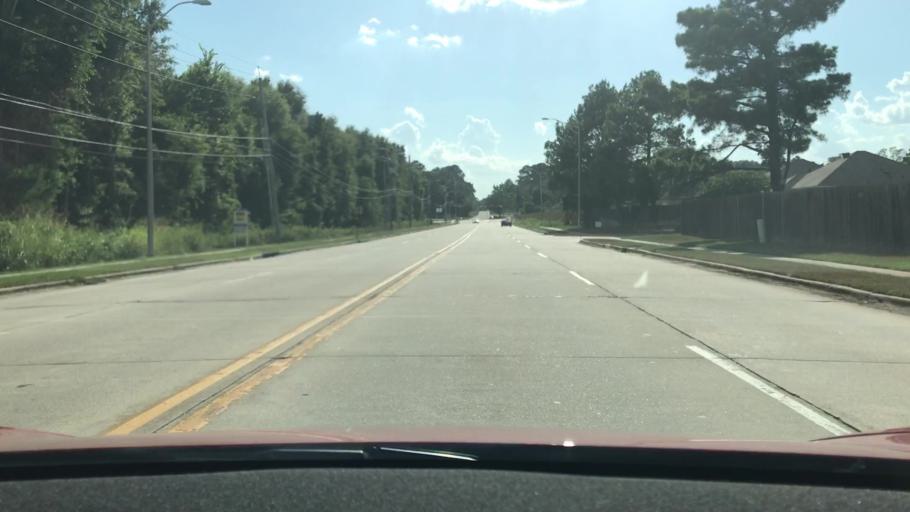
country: US
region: Louisiana
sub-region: Bossier Parish
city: Bossier City
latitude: 32.4130
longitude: -93.7762
